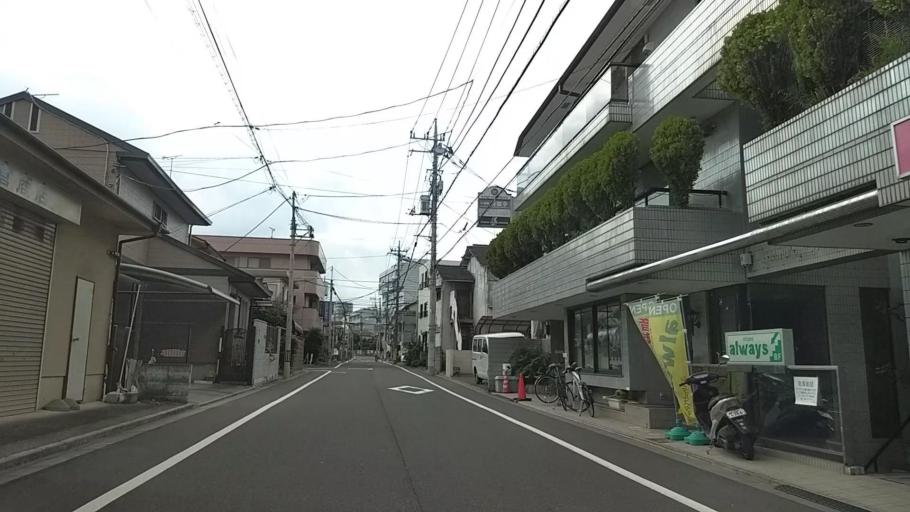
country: JP
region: Tokyo
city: Hachioji
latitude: 35.6577
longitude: 139.3209
